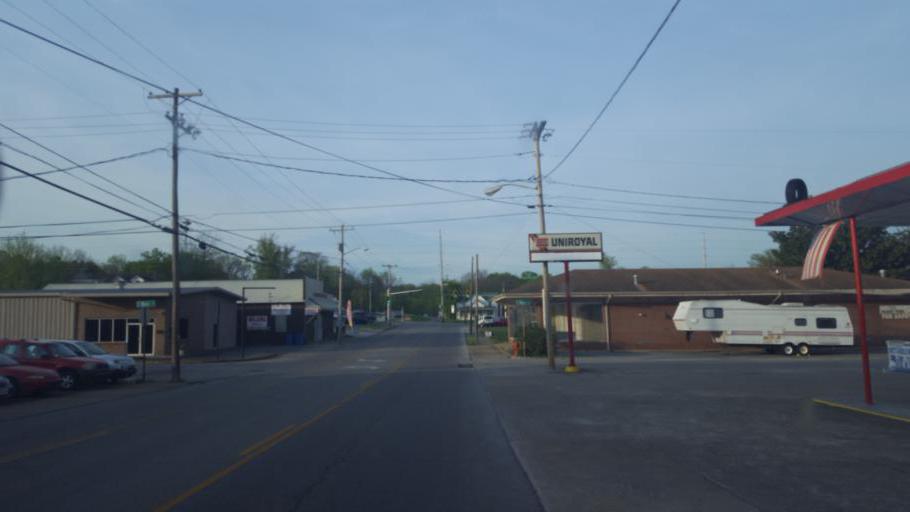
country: US
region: Kentucky
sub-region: Barren County
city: Glasgow
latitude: 36.9960
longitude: -85.9103
